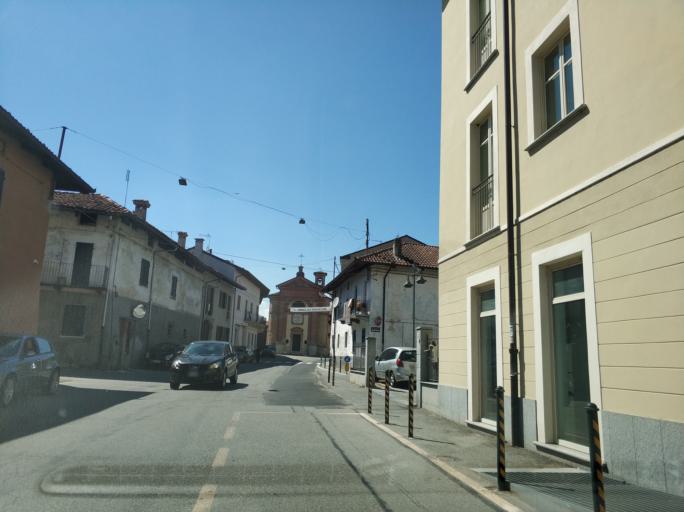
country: IT
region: Piedmont
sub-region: Provincia di Torino
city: San Benigno Canavese
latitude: 45.2242
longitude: 7.7815
